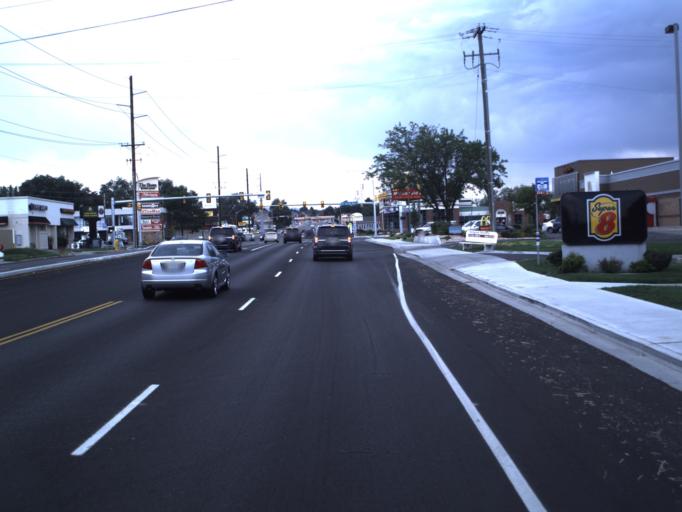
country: US
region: Utah
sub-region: Salt Lake County
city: Midvale
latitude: 40.6235
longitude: -111.8661
